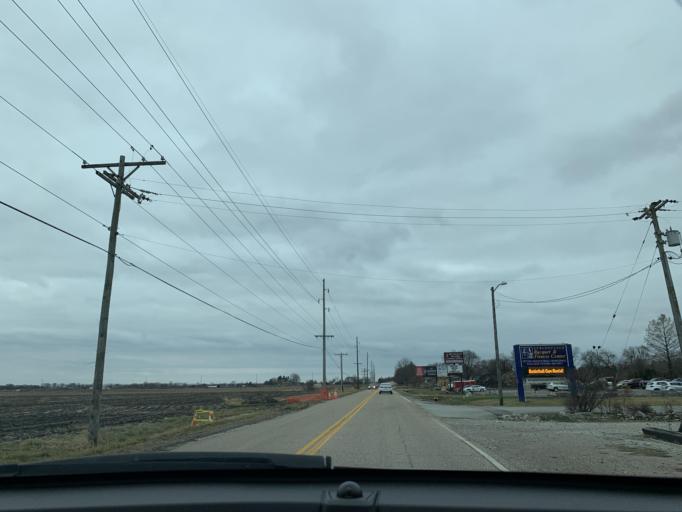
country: US
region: Illinois
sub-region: Sangamon County
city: Jerome
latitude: 39.7514
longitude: -89.6867
